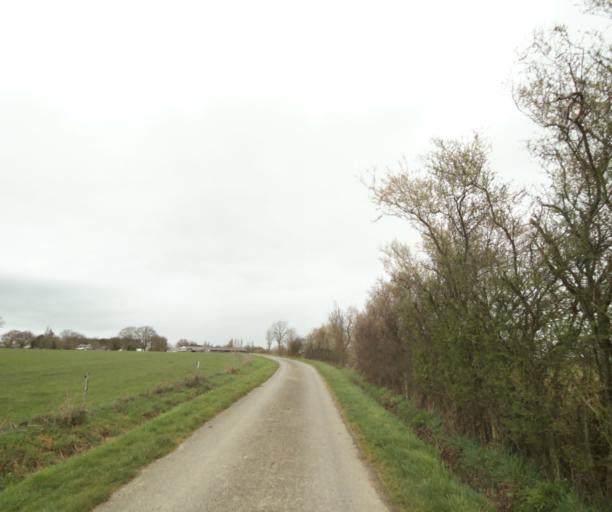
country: FR
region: Pays de la Loire
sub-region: Departement de la Loire-Atlantique
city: Bouvron
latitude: 47.4311
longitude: -1.8466
